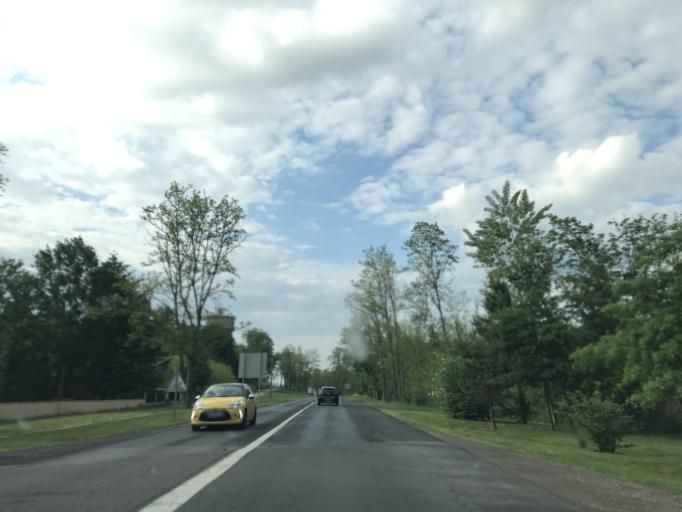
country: FR
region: Auvergne
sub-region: Departement du Puy-de-Dome
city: Lezoux
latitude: 45.8493
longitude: 3.3928
